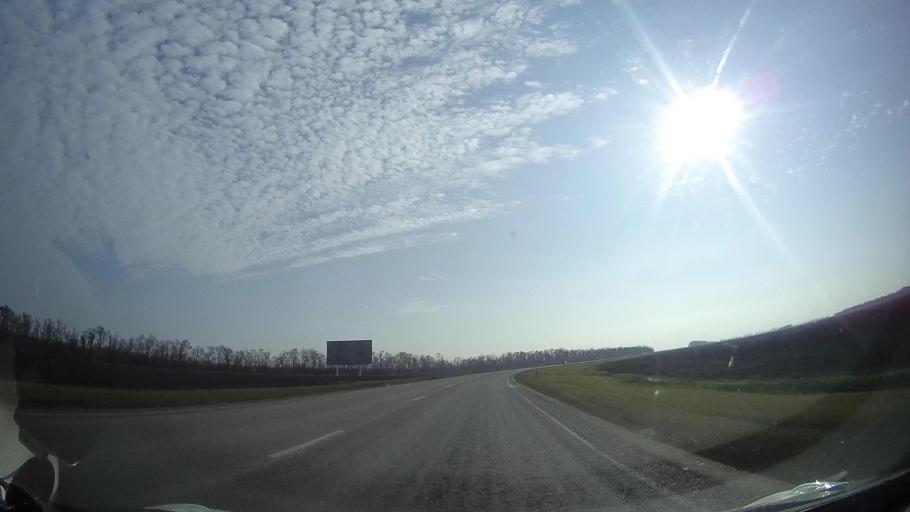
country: RU
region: Rostov
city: Tselina
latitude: 46.5308
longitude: 40.9879
